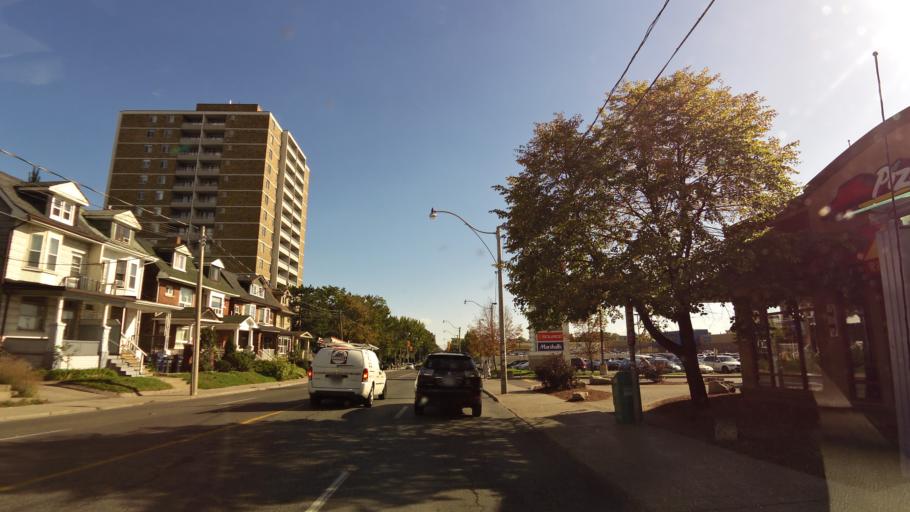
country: CA
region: Ontario
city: Toronto
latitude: 43.6581
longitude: -79.4347
